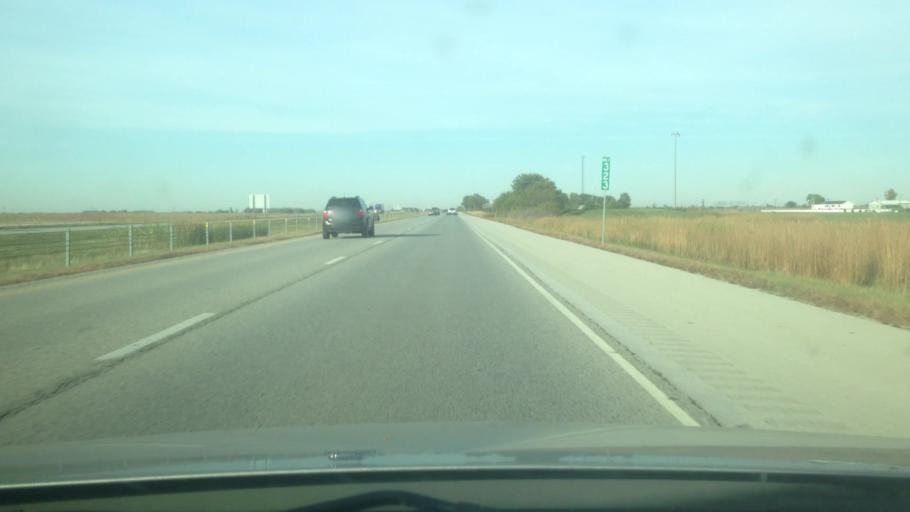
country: US
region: Illinois
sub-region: Kankakee County
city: Manteno
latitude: 41.2675
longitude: -87.8439
